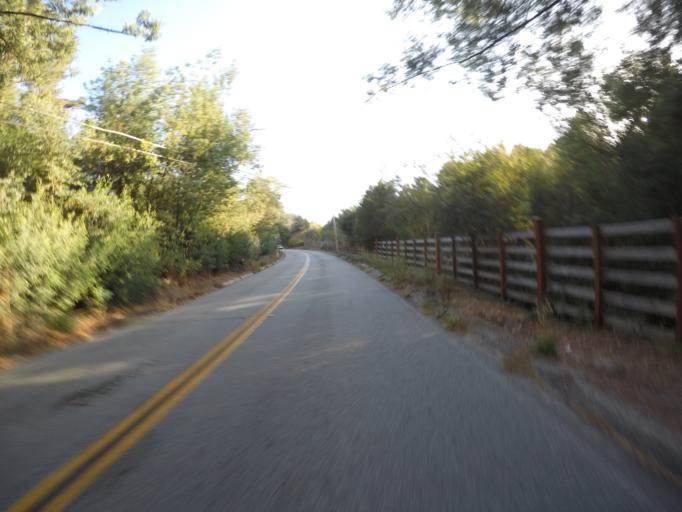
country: US
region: California
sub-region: Santa Cruz County
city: Pasatiempo
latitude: 37.0184
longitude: -122.0286
